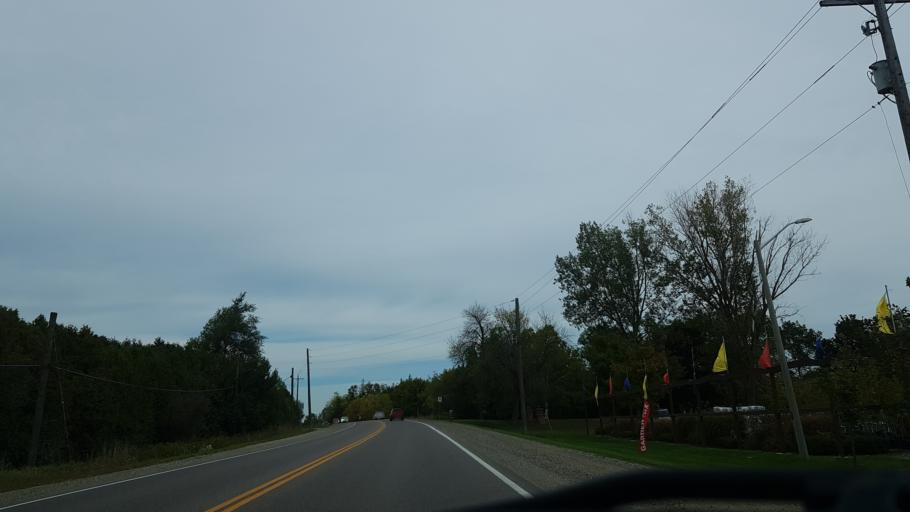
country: CA
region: Ontario
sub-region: Wellington County
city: Guelph
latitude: 43.5957
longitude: -80.2365
